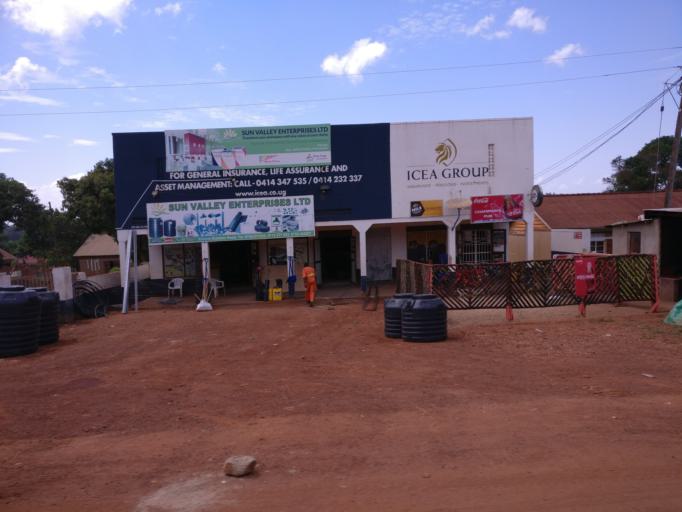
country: UG
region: Central Region
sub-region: Wakiso District
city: Kajansi
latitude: 0.1866
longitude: 32.5388
